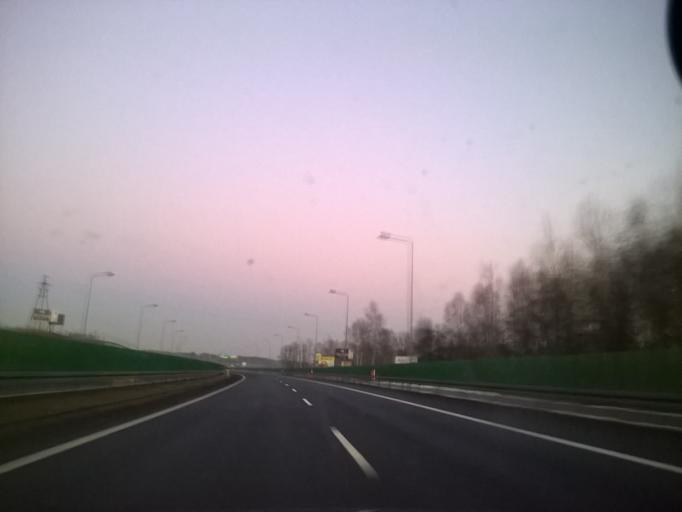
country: PL
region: Warmian-Masurian Voivodeship
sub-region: Powiat olsztynski
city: Barczewo
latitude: 53.8261
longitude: 20.8075
